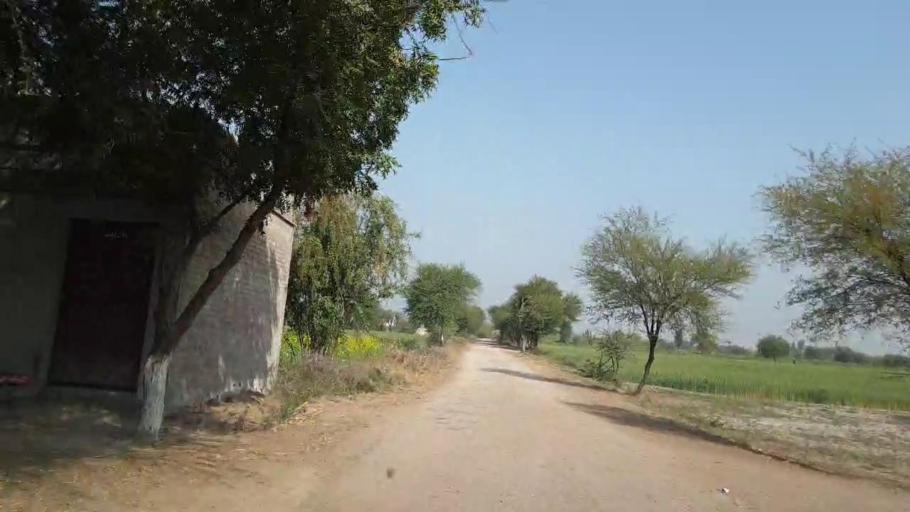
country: PK
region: Sindh
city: Mirpur Khas
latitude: 25.5844
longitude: 69.0125
